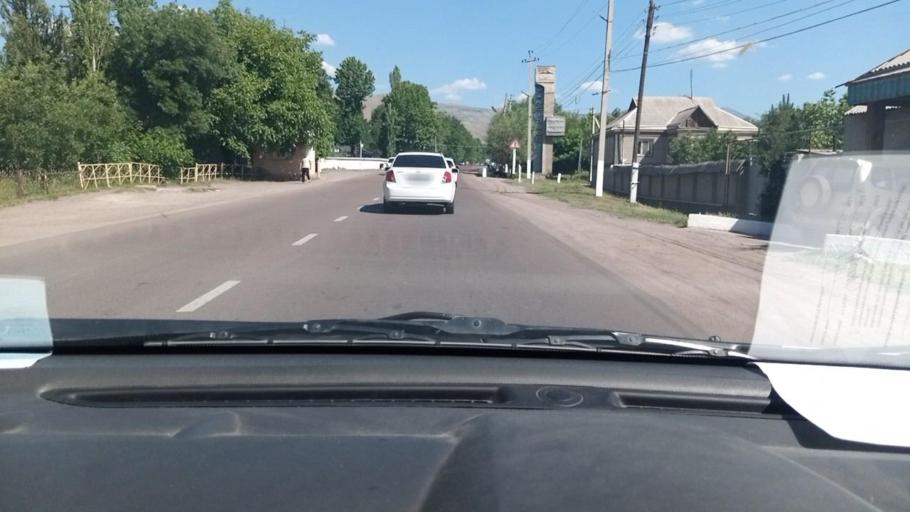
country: UZ
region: Toshkent
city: Angren
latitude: 41.0393
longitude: 70.0940
